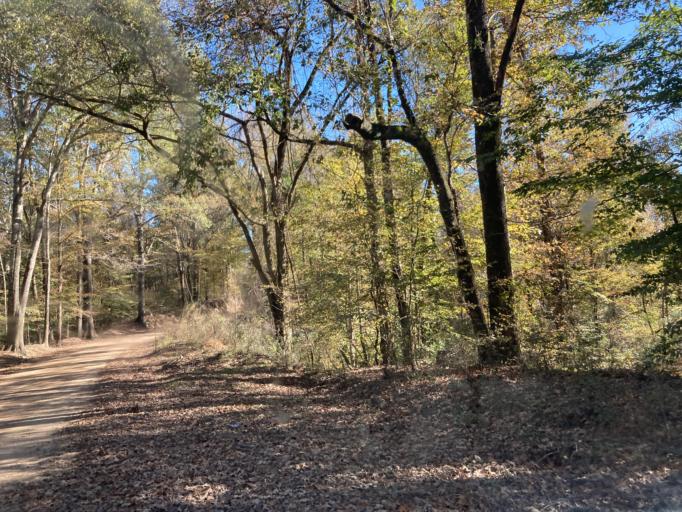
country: US
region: Mississippi
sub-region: Yazoo County
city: Yazoo City
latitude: 32.7768
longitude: -90.4074
